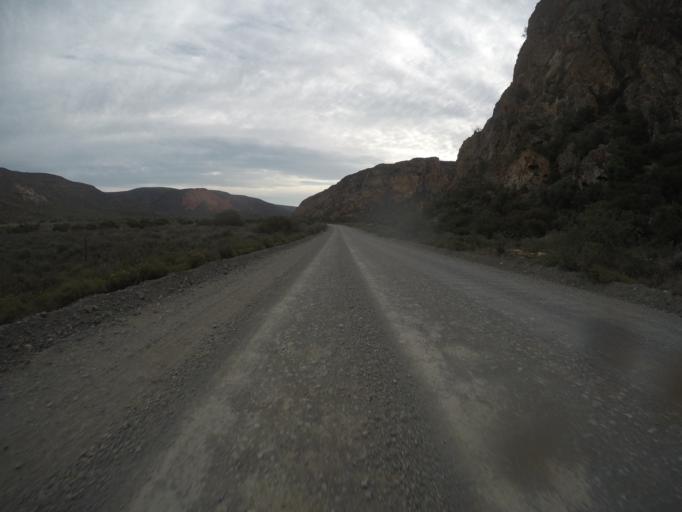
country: ZA
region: Eastern Cape
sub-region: Cacadu District Municipality
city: Willowmore
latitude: -33.5206
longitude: 23.6643
